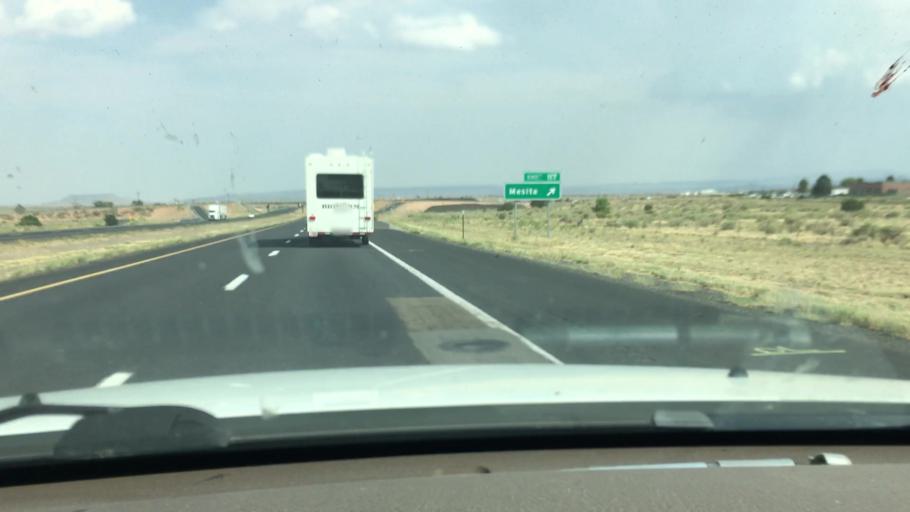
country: US
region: New Mexico
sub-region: Cibola County
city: Laguna
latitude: 35.0153
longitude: -107.3263
